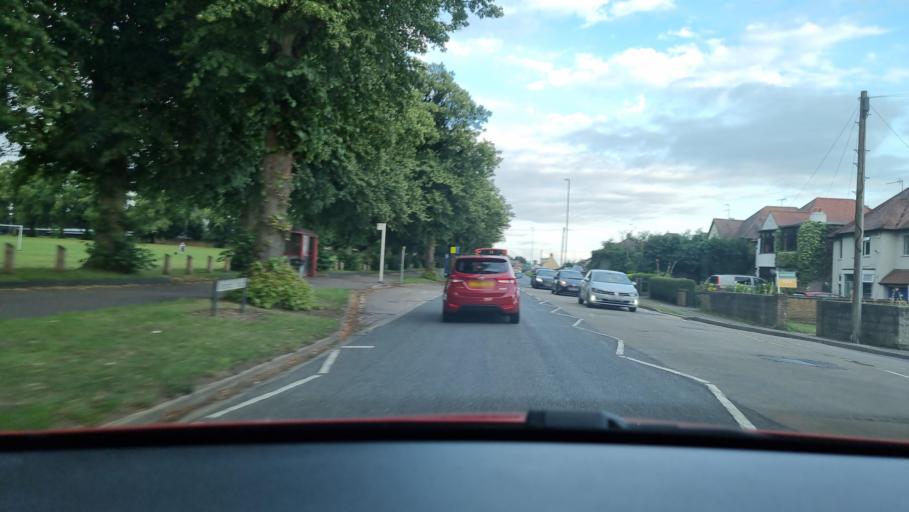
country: GB
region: England
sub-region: Northamptonshire
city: Northampton
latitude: 52.2660
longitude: -0.9051
